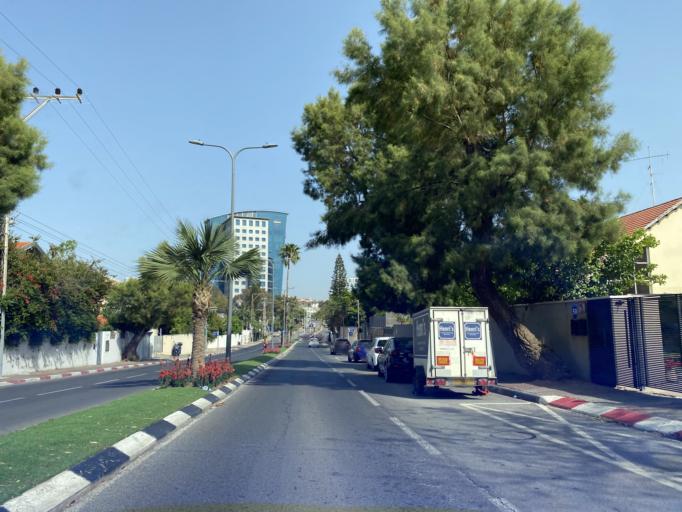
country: IL
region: Tel Aviv
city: Herzliya Pituah
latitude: 32.1674
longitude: 34.8070
